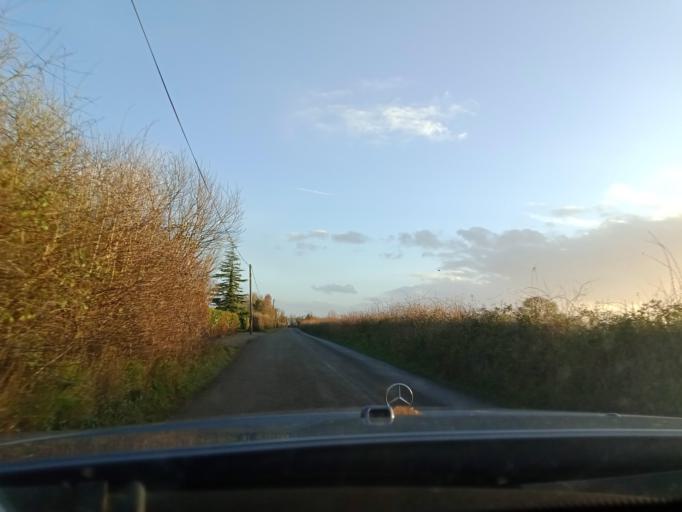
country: IE
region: Leinster
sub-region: Kilkenny
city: Callan
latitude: 52.5031
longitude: -7.3417
